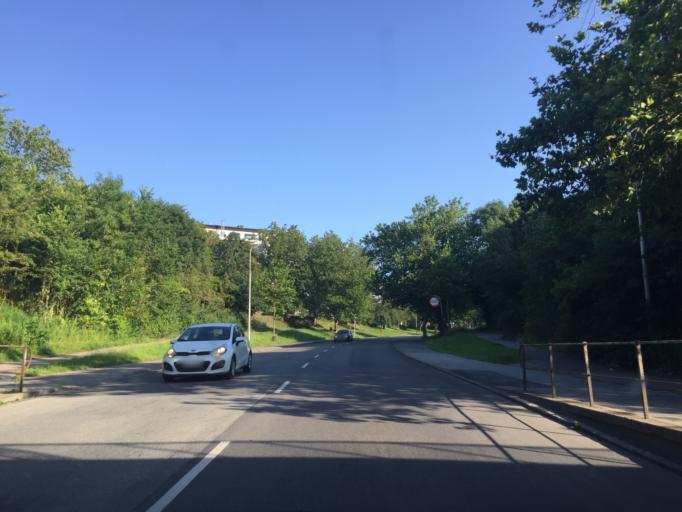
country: DK
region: Capital Region
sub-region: Kobenhavn
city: Copenhagen
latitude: 55.7109
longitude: 12.5539
